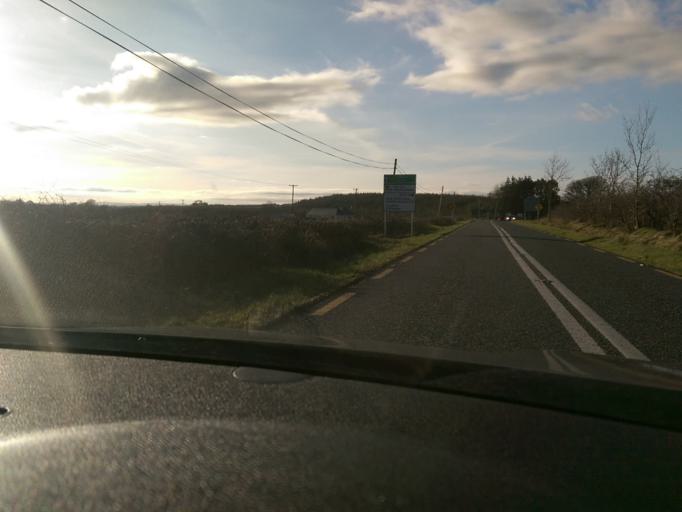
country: IE
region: Connaught
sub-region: Roscommon
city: Boyle
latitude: 53.9055
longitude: -8.2616
